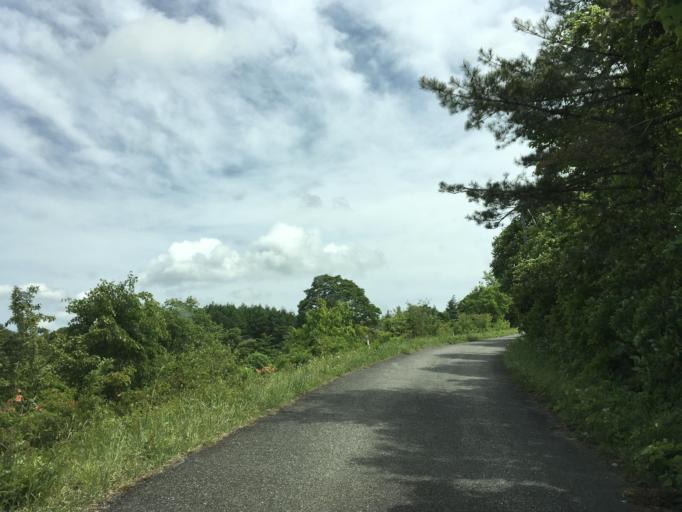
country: JP
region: Iwate
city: Mizusawa
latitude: 39.1329
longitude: 141.3166
